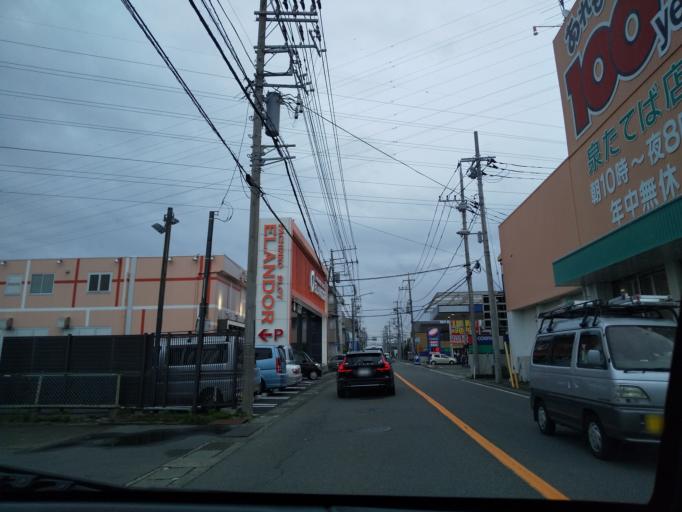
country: JP
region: Kanagawa
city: Fujisawa
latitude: 35.4032
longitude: 139.5014
